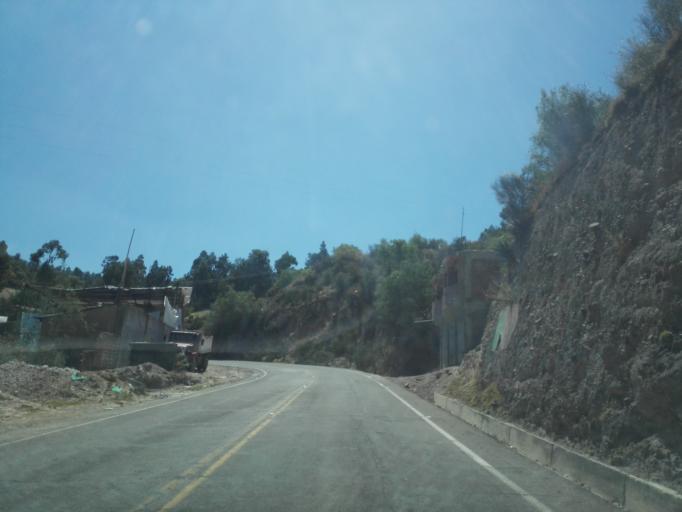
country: PE
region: Ayacucho
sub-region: Provincia de Huamanga
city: Ayacucho
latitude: -13.1646
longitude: -74.2416
